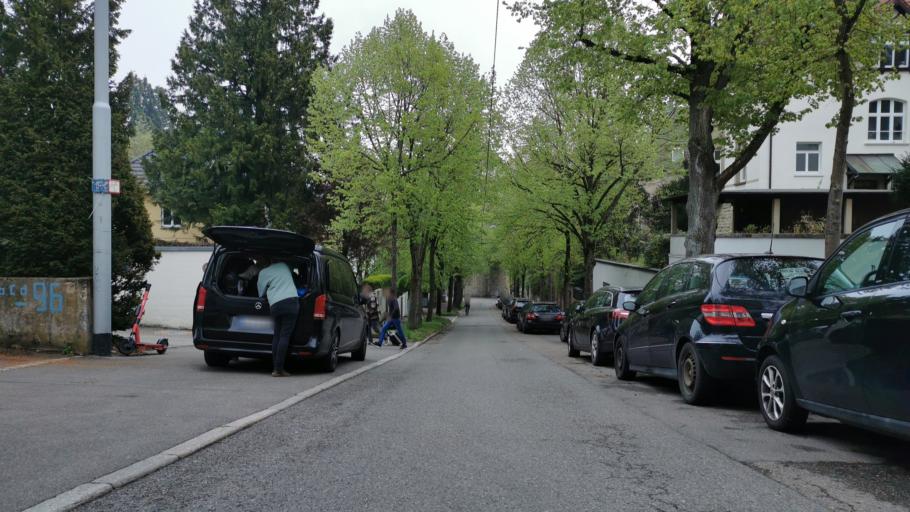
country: DE
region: Baden-Wuerttemberg
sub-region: Regierungsbezirk Stuttgart
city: Stuttgart
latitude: 48.7861
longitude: 9.1572
